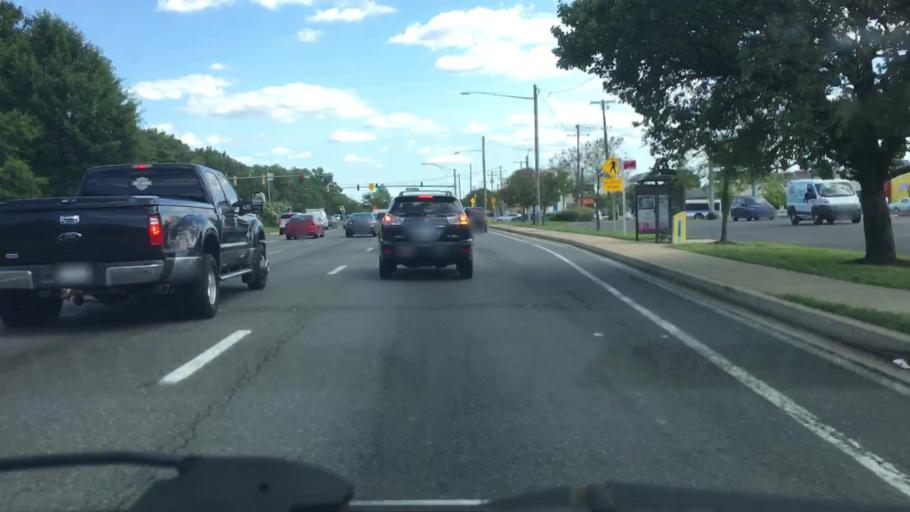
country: US
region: Maryland
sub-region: Prince George's County
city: Silver Hill
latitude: 38.8404
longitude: -76.9474
